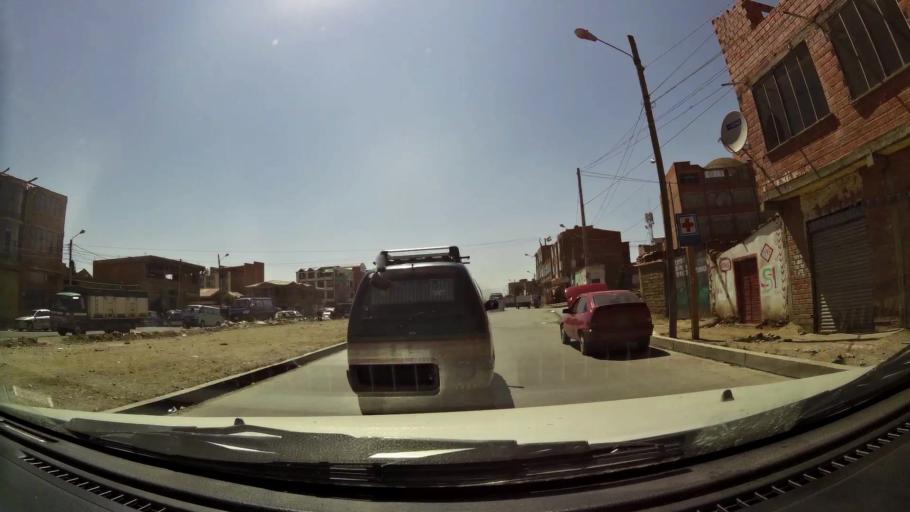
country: BO
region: La Paz
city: La Paz
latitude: -16.5340
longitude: -68.1639
